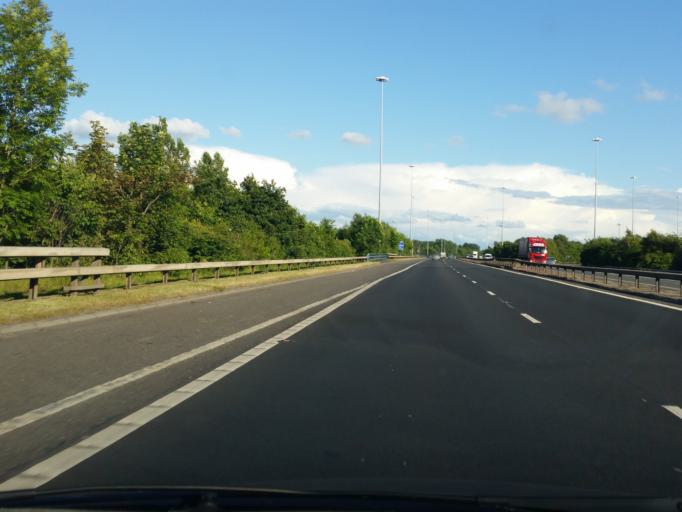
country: GB
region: Scotland
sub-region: South Lanarkshire
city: Hamilton
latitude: 55.7830
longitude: -4.0248
